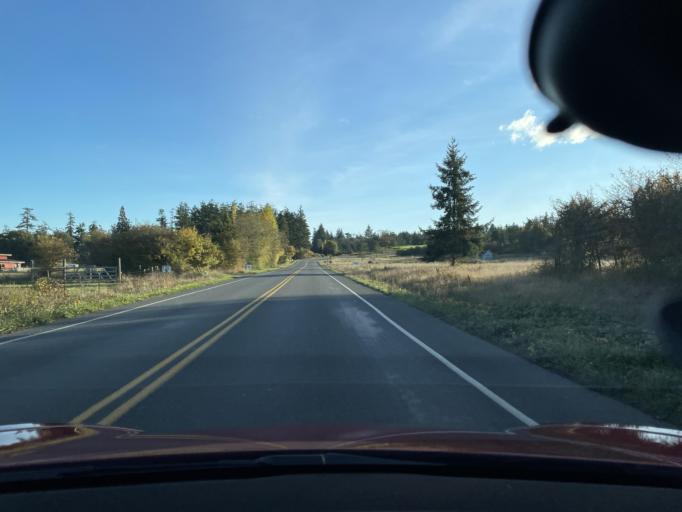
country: US
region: Washington
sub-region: San Juan County
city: Friday Harbor
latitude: 48.5138
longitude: -123.0231
